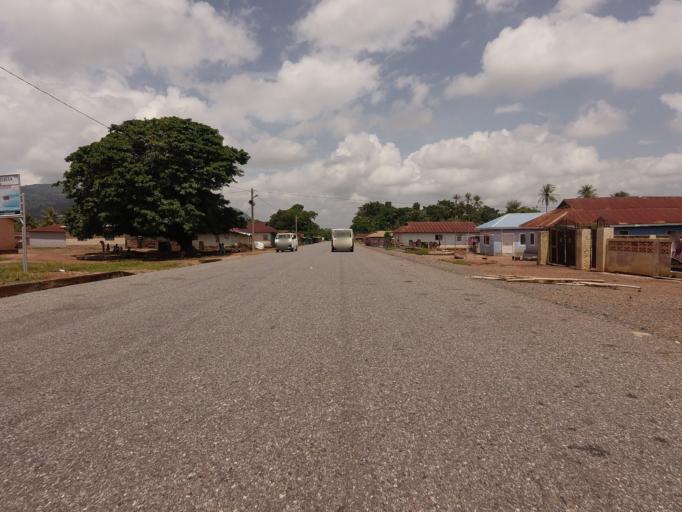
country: GH
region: Volta
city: Kpandu
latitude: 6.8483
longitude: 0.3925
